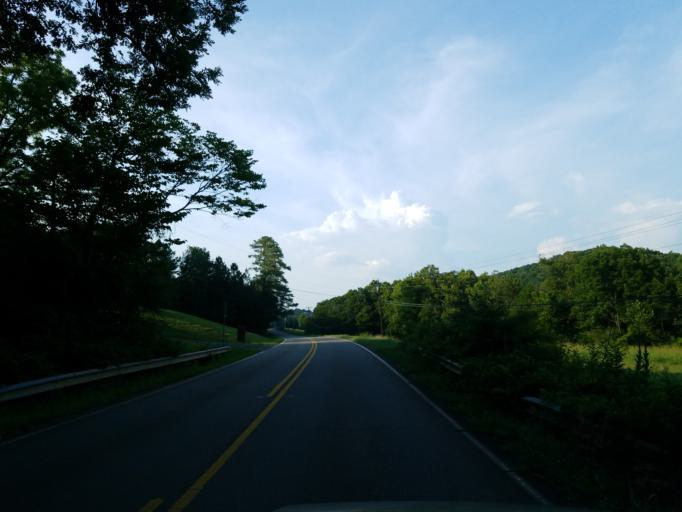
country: US
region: Georgia
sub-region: Pickens County
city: Jasper
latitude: 34.5557
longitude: -84.5393
